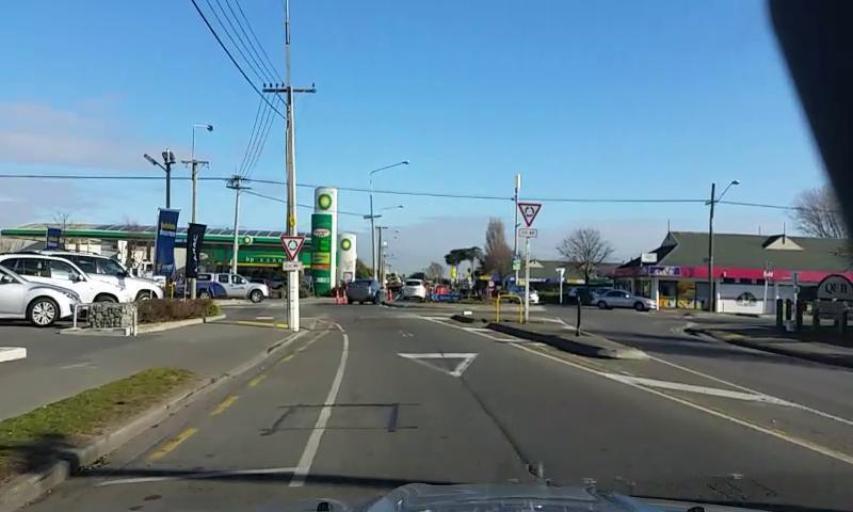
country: NZ
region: Canterbury
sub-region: Christchurch City
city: Christchurch
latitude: -43.4953
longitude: 172.7114
